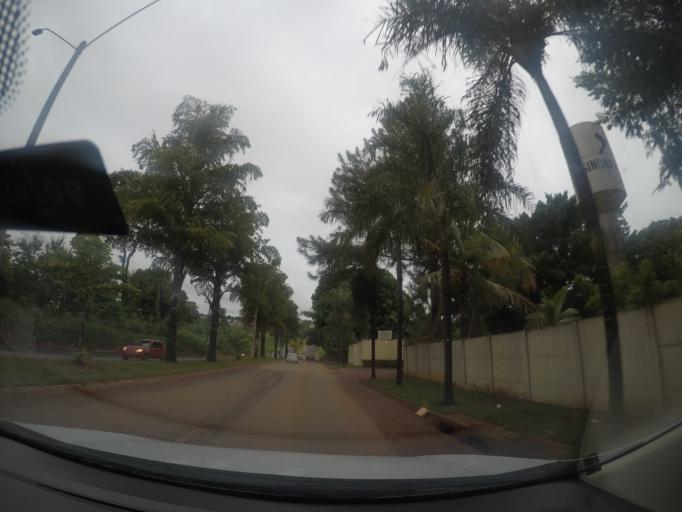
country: BR
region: Goias
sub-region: Aparecida De Goiania
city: Aparecida de Goiania
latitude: -16.7591
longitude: -49.3224
